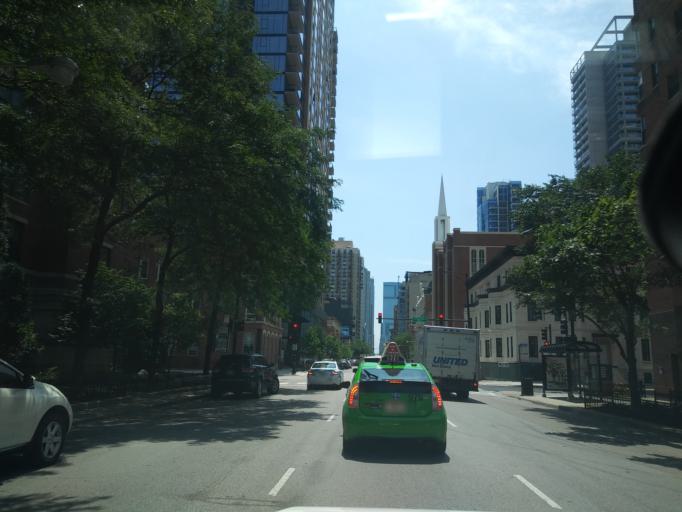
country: US
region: Illinois
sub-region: Cook County
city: Chicago
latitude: 41.8984
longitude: -87.6313
